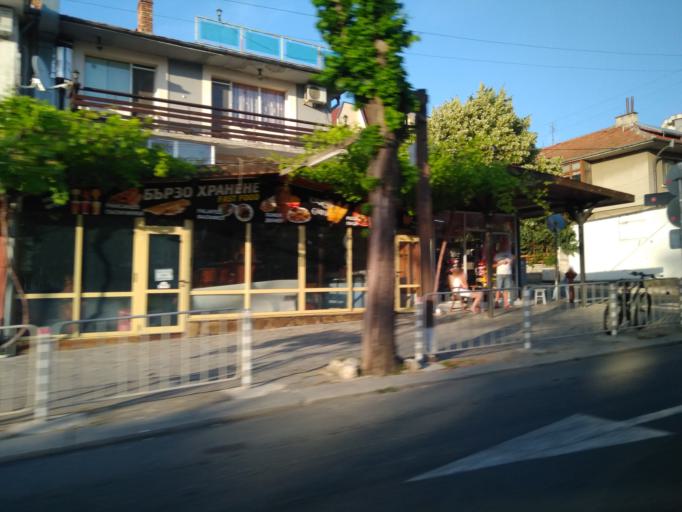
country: BG
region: Burgas
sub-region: Obshtina Nesebur
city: Nesebar
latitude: 42.6636
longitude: 27.7172
